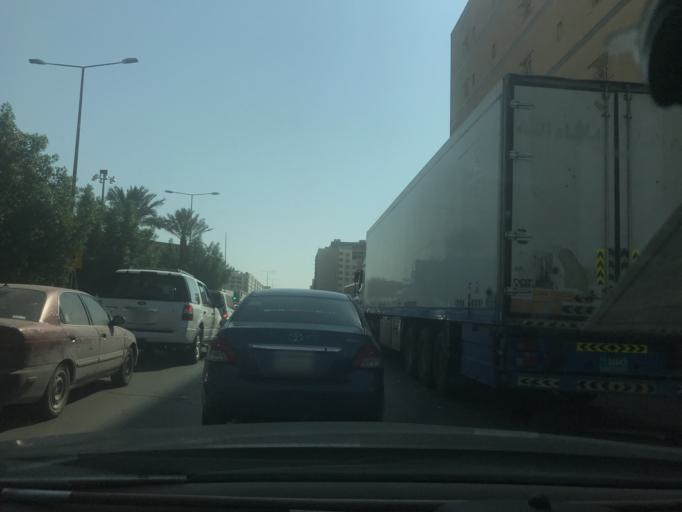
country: SA
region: Ar Riyad
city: Riyadh
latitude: 24.6476
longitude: 46.7145
